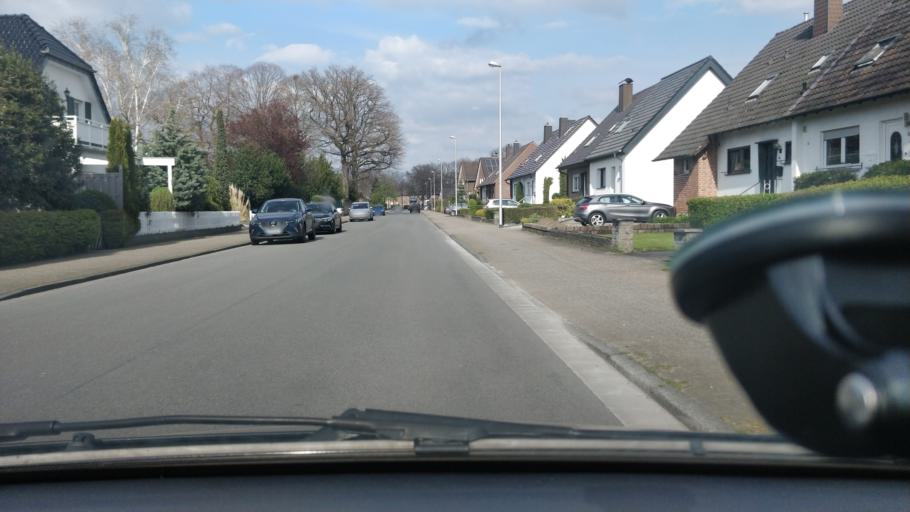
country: DE
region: North Rhine-Westphalia
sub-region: Regierungsbezirk Dusseldorf
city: Bocholt
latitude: 51.8493
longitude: 6.6308
